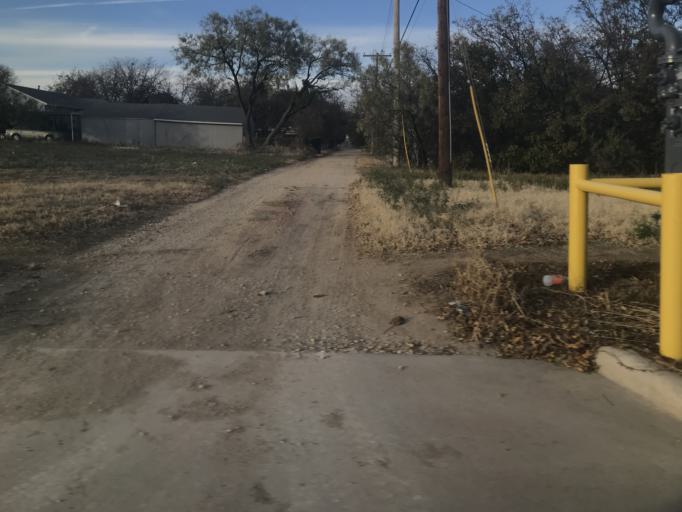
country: US
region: Texas
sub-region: Taylor County
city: Abilene
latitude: 32.4322
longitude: -99.7426
